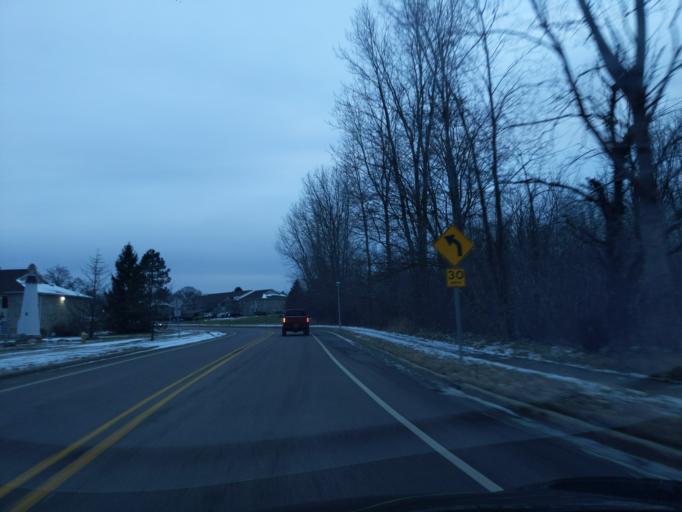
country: US
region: Michigan
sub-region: Ingham County
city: Mason
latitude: 42.5713
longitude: -84.4498
